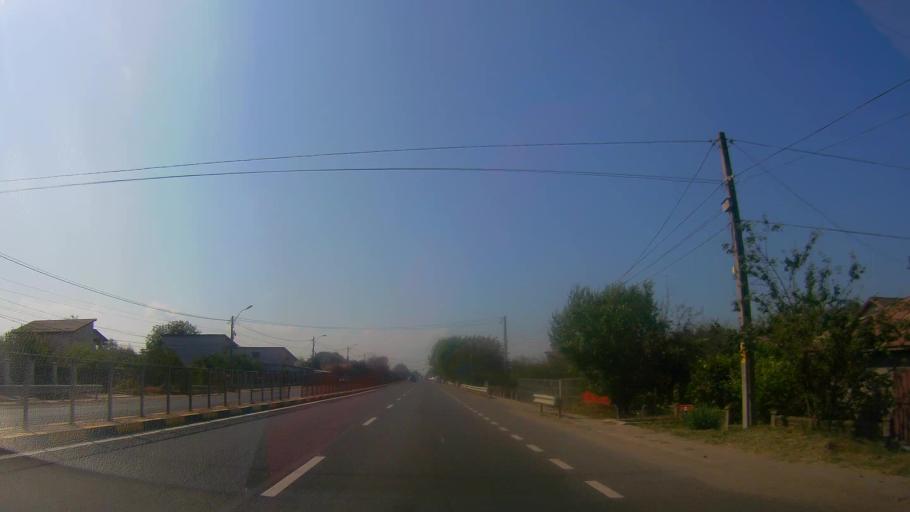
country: RO
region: Giurgiu
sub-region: Comuna Fratesti
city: Remus
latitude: 43.9396
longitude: 25.9780
